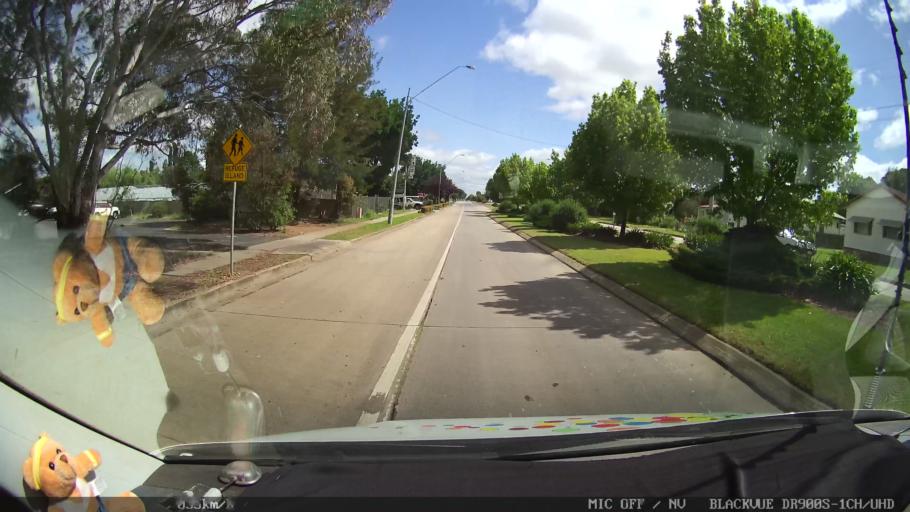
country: AU
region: New South Wales
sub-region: Glen Innes Severn
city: Glen Innes
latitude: -29.7472
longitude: 151.7364
